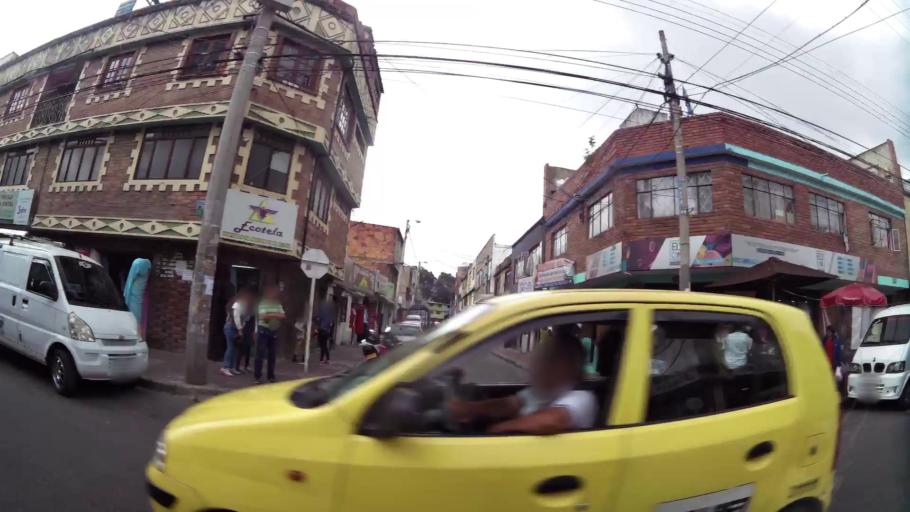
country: CO
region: Bogota D.C.
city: Bogota
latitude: 4.5874
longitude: -74.0887
